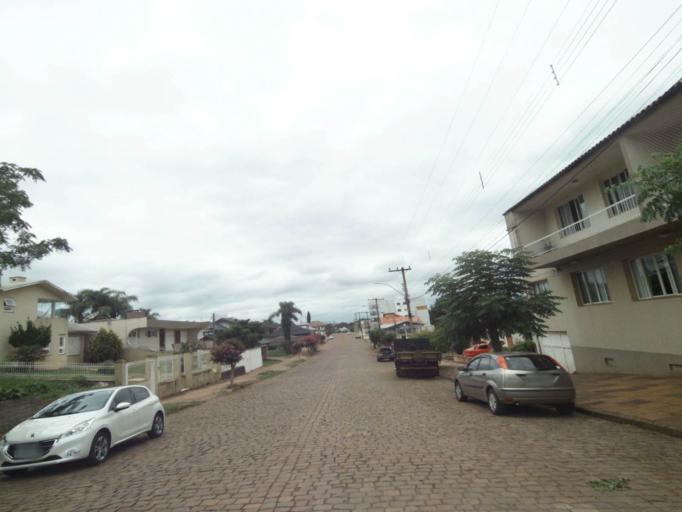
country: BR
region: Rio Grande do Sul
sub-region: Lagoa Vermelha
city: Lagoa Vermelha
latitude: -28.2069
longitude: -51.5215
